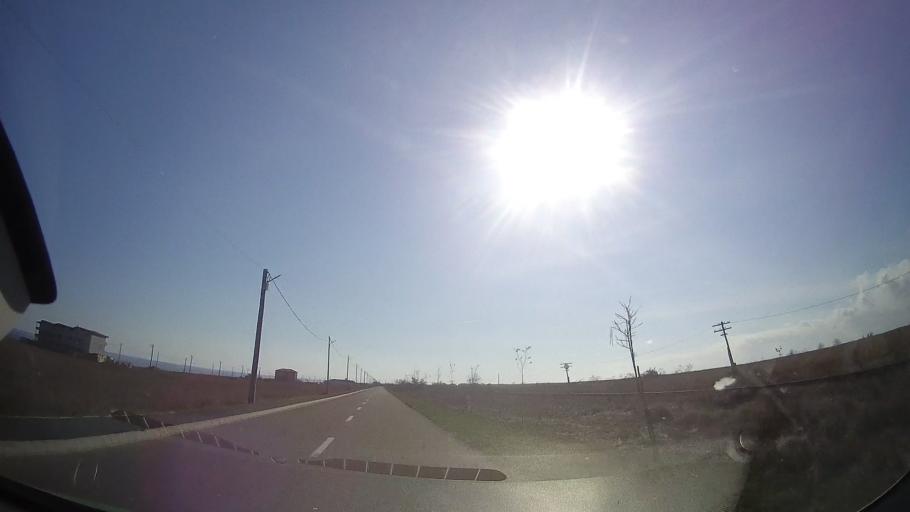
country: RO
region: Constanta
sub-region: Comuna Costinesti
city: Schitu
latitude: 43.9321
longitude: 28.6313
